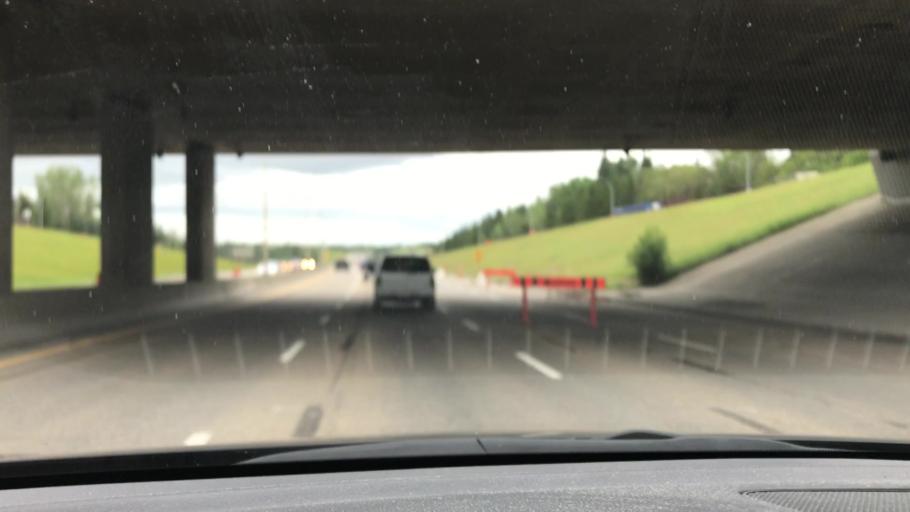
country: CA
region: Alberta
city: Edmonton
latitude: 53.4828
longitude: -113.5409
